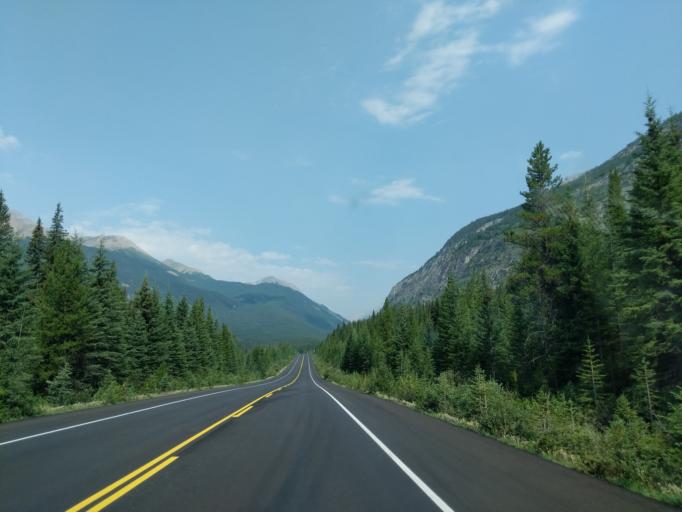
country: CA
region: British Columbia
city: Golden
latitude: 52.1006
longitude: -116.9578
